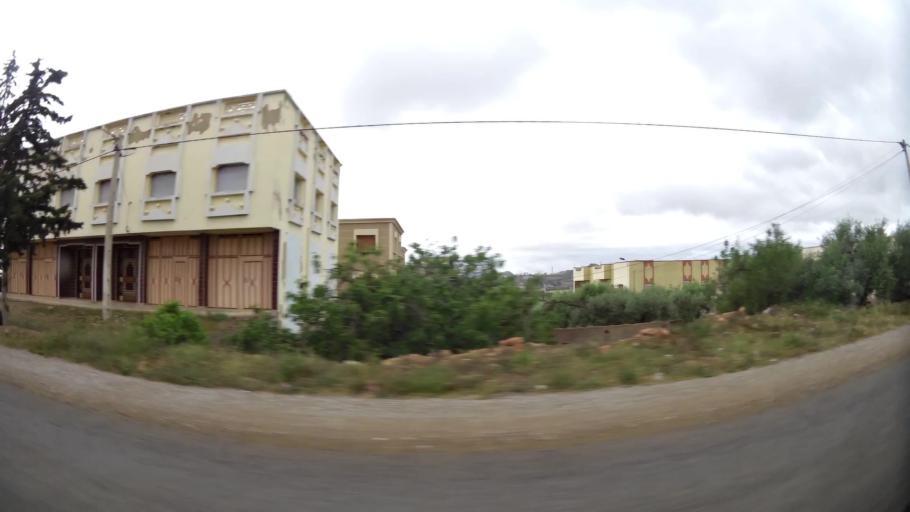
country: MA
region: Oriental
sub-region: Nador
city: Midar
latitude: 35.0582
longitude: -3.4672
